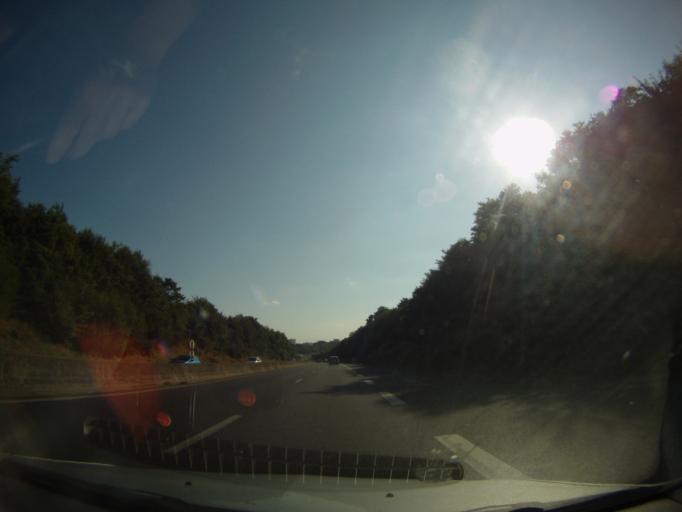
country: FR
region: Pays de la Loire
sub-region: Departement de la Loire-Atlantique
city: La Chapelle-sur-Erdre
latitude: 47.2734
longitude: -1.5532
